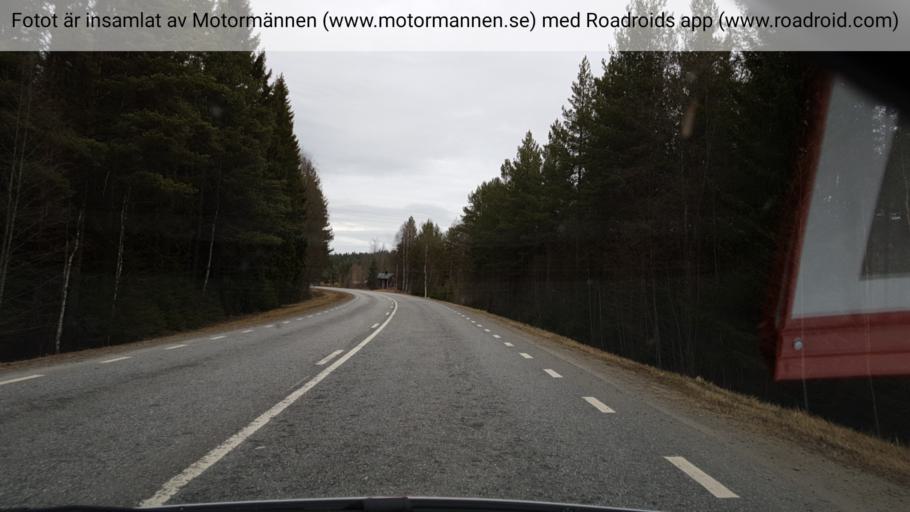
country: SE
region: Vaesternorrland
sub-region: Solleftea Kommun
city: Solleftea
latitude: 63.2560
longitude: 17.2190
